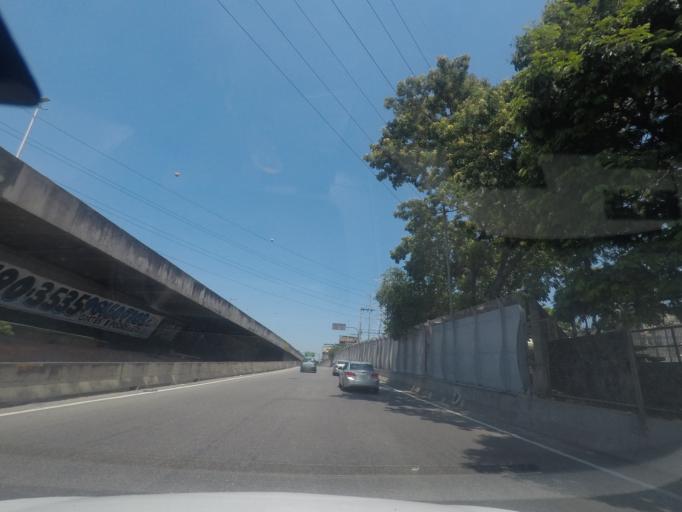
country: BR
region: Rio de Janeiro
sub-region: Rio De Janeiro
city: Rio de Janeiro
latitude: -22.8718
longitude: -43.2577
